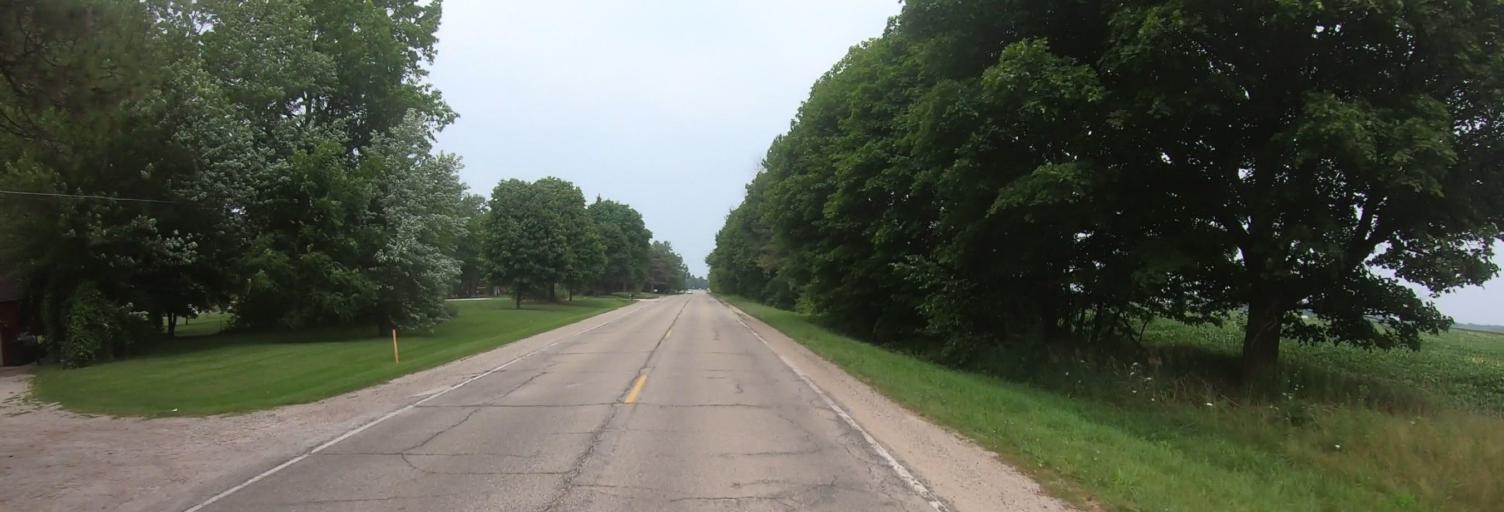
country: US
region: Michigan
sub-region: Shiawassee County
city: Durand
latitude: 42.9133
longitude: -84.0322
